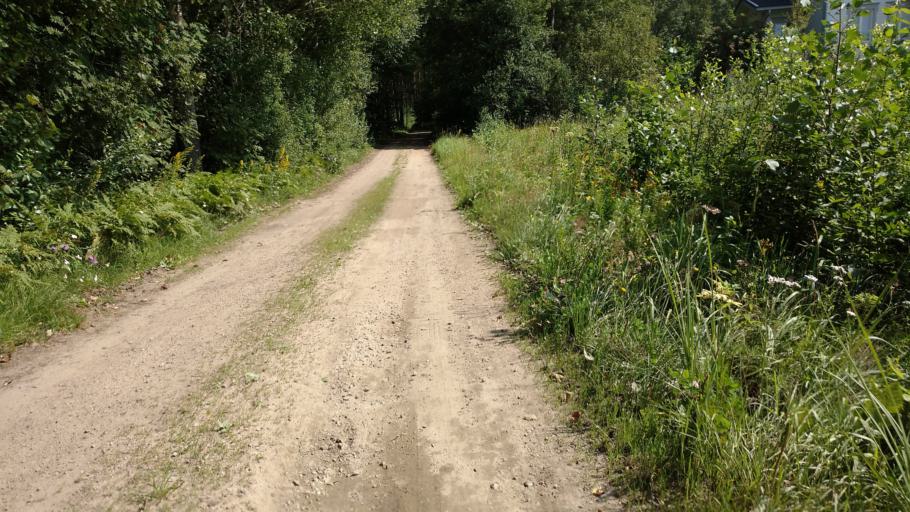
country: FI
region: Varsinais-Suomi
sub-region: Salo
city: Salo
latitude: 60.4081
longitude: 23.1965
